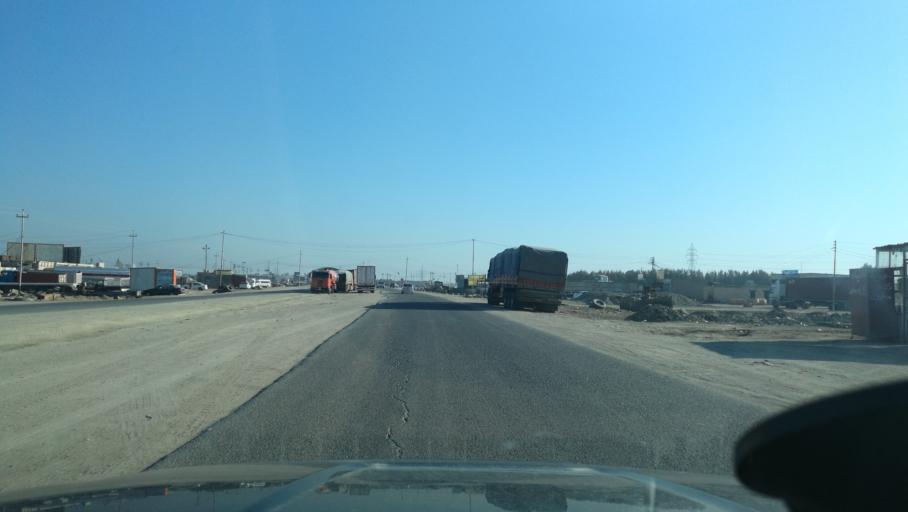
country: IQ
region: Dhi Qar
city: An Nasiriyah
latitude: 31.0008
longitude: 46.2573
